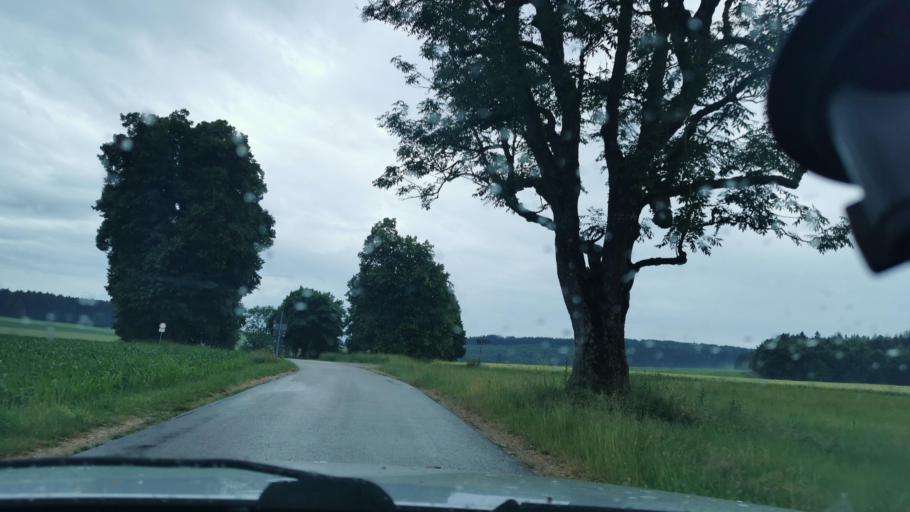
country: DE
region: Baden-Wuerttemberg
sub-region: Regierungsbezirk Stuttgart
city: Bohmenkirch
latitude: 48.7173
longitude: 9.9213
